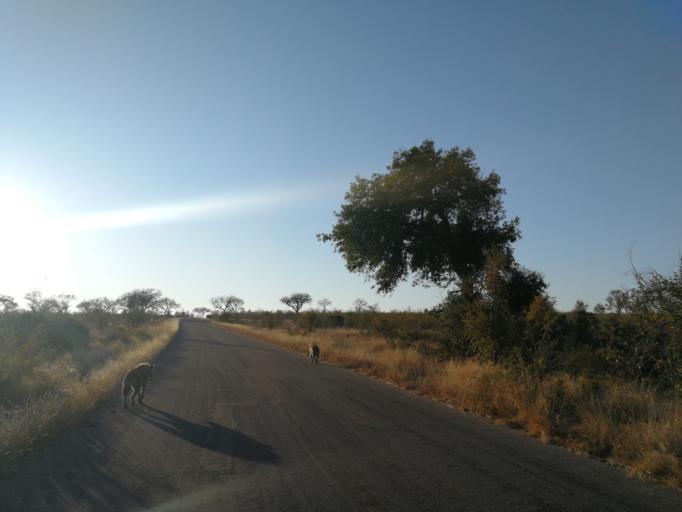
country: ZA
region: Limpopo
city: Thulamahashi
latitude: -25.0289
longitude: 31.3624
